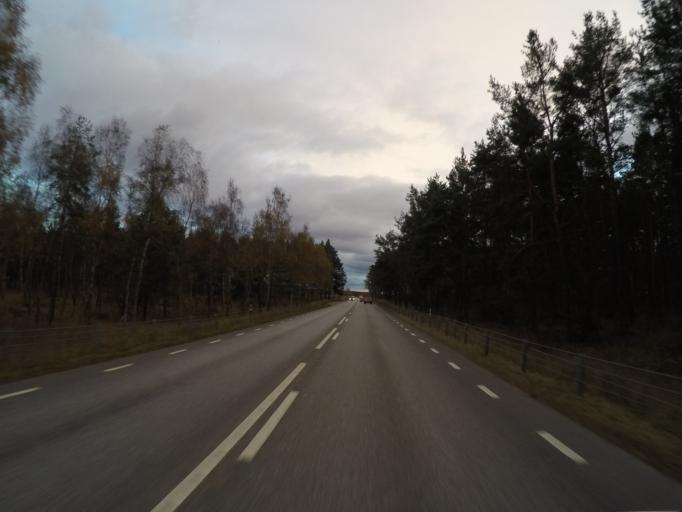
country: SE
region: Skane
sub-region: Kristianstads Kommun
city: Norra Asum
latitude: 55.9440
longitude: 14.0688
